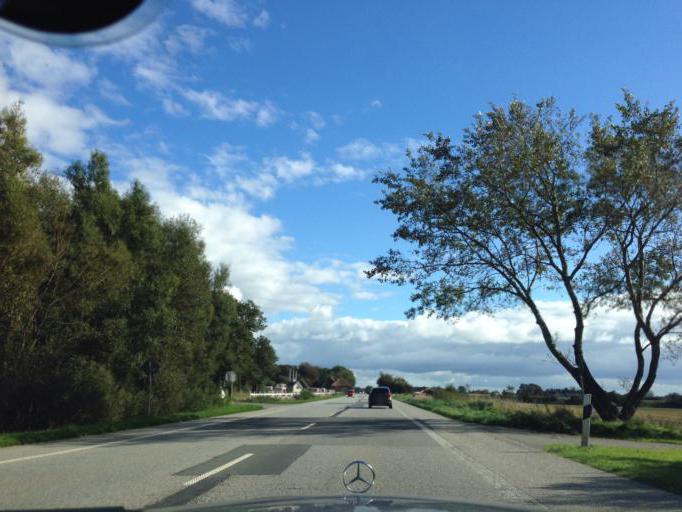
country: DE
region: Schleswig-Holstein
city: Risum-Lindholm
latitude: 54.7691
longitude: 8.8631
